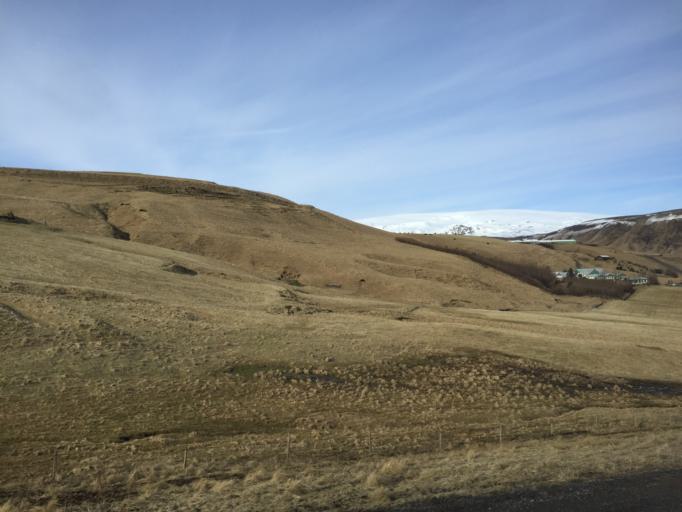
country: IS
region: South
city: Vestmannaeyjar
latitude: 63.4406
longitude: -19.1473
